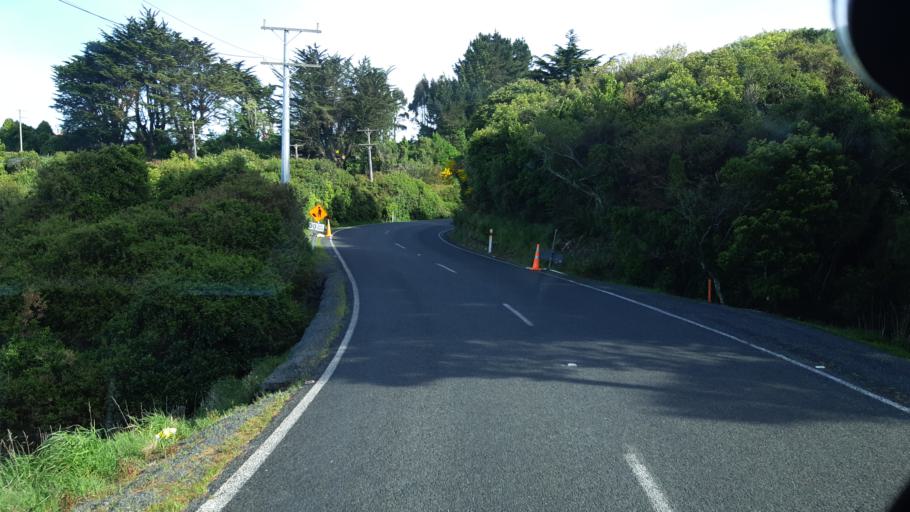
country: NZ
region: Otago
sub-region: Dunedin City
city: Portobello
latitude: -45.8763
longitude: 170.6258
